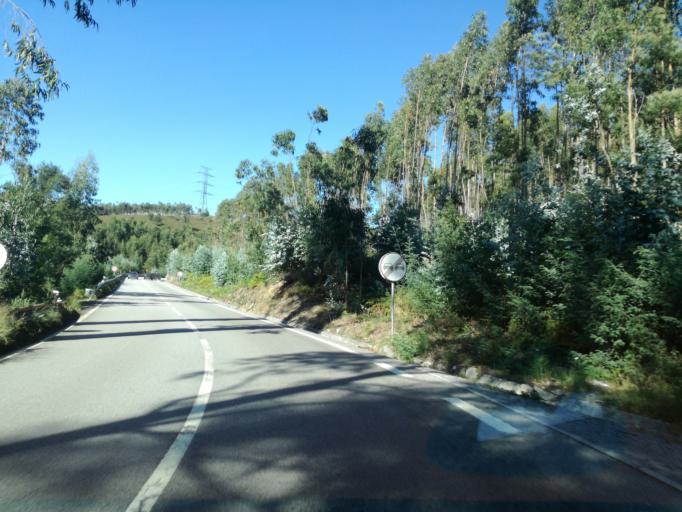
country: PT
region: Porto
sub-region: Pacos de Ferreira
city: Seroa
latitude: 41.2561
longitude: -8.4611
